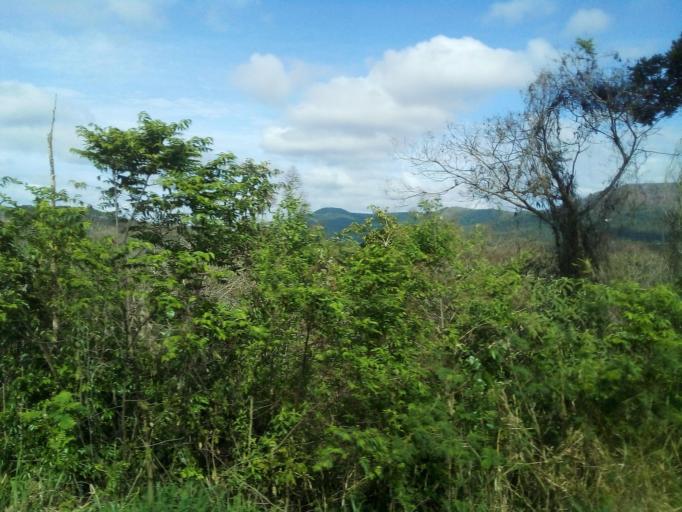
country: BR
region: Minas Gerais
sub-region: Raposos
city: Raposos
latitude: -19.8805
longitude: -43.7654
